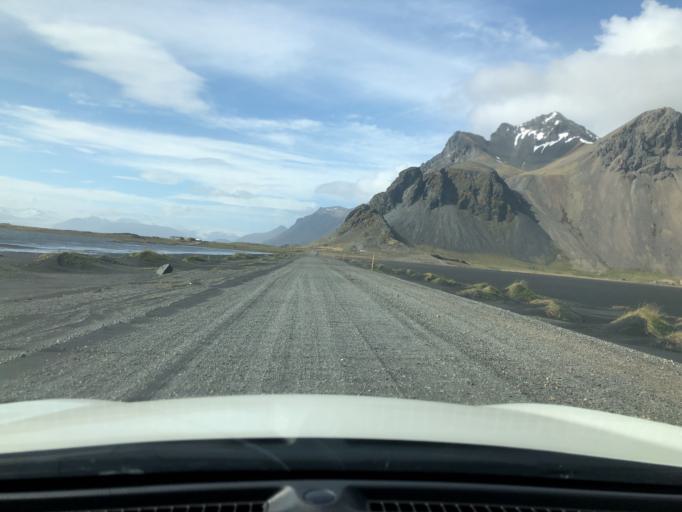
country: IS
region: East
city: Hoefn
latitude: 64.2477
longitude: -14.9794
